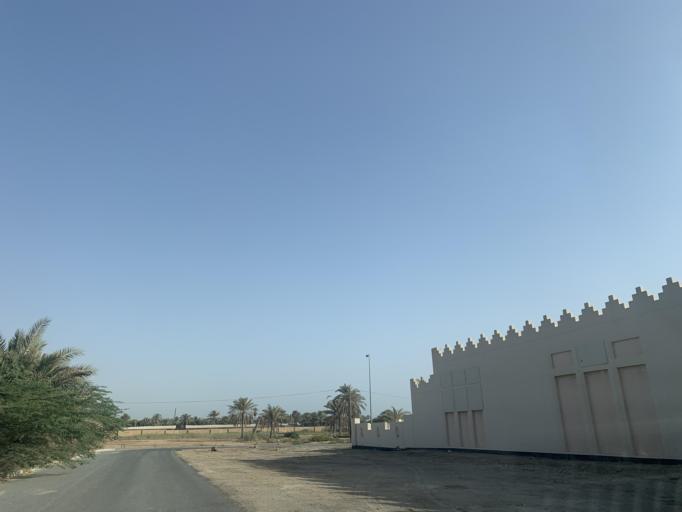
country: BH
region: Central Governorate
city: Madinat Hamad
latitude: 26.1900
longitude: 50.4584
